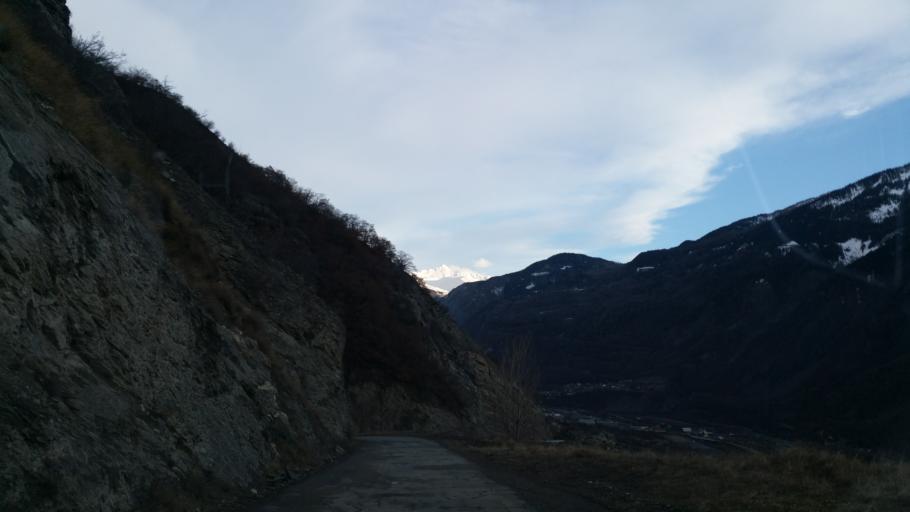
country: FR
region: Rhone-Alpes
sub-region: Departement de la Savoie
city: Villargondran
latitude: 45.2718
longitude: 6.3825
